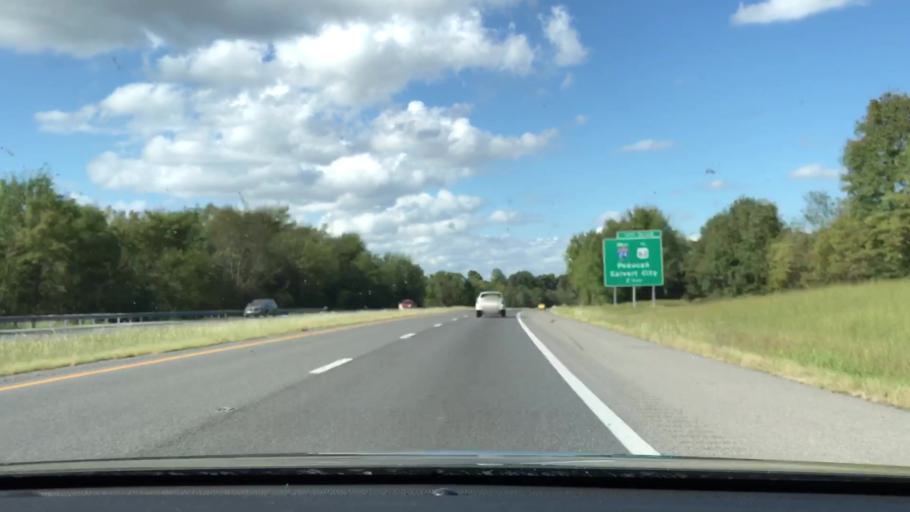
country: US
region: Kentucky
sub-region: Marshall County
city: Calvert City
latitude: 36.9480
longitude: -88.3495
